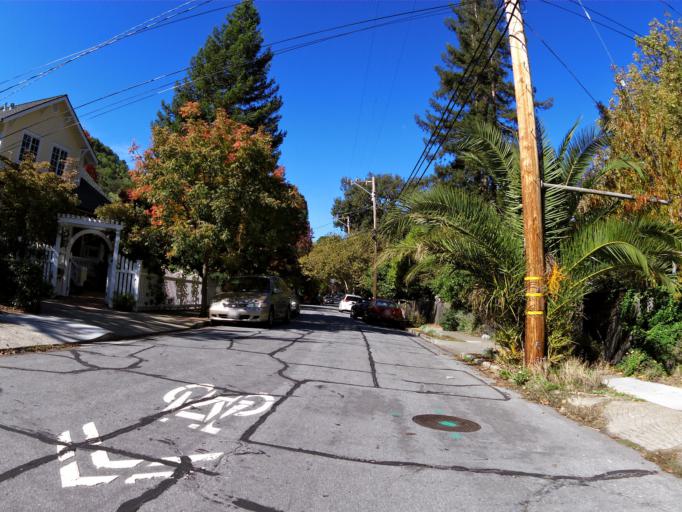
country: US
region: California
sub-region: Marin County
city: San Anselmo
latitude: 37.9801
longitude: -122.5748
